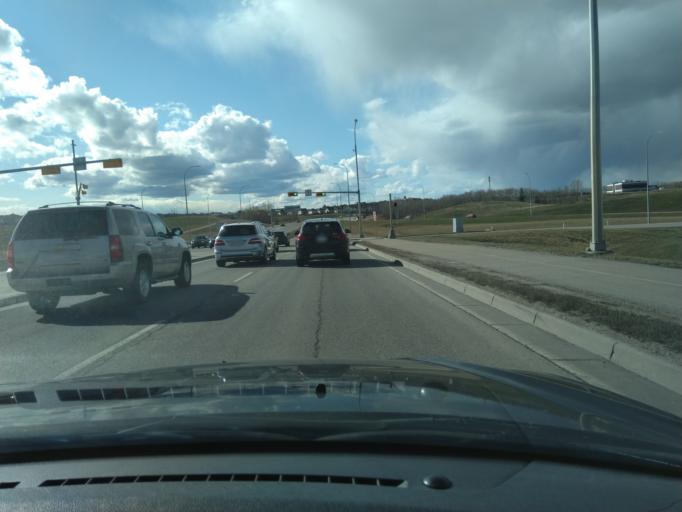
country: CA
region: Alberta
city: Calgary
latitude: 51.1452
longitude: -114.2048
